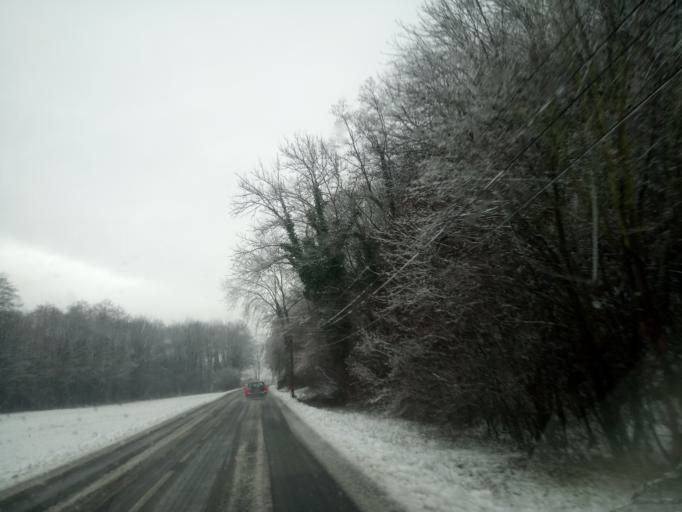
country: FR
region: Rhone-Alpes
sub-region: Departement de la Savoie
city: Saint-Remy-de-Maurienne
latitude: 45.3783
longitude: 6.2729
